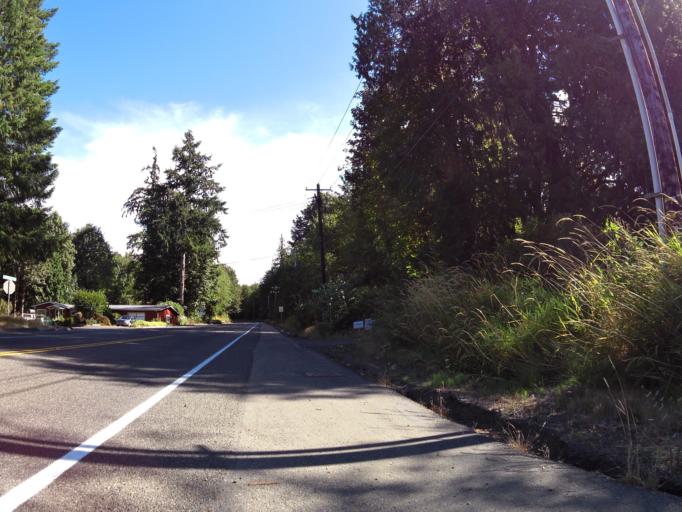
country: US
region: Washington
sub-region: Mason County
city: Shelton
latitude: 47.1258
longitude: -123.0920
